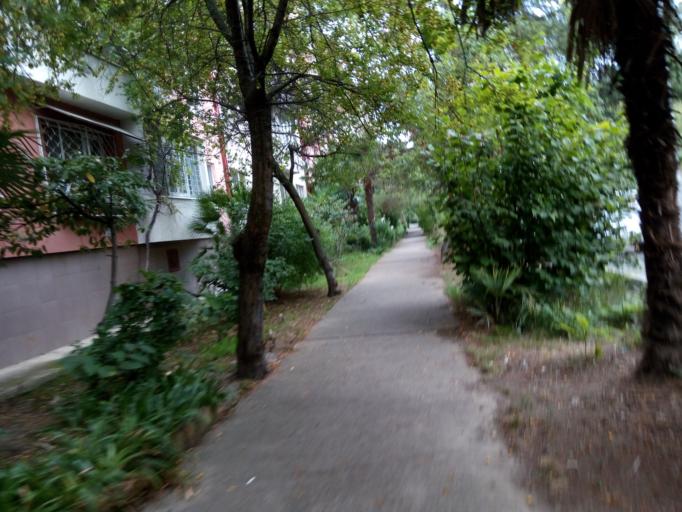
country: RU
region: Krasnodarskiy
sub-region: Sochi City
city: Sochi
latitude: 43.5663
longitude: 39.7605
